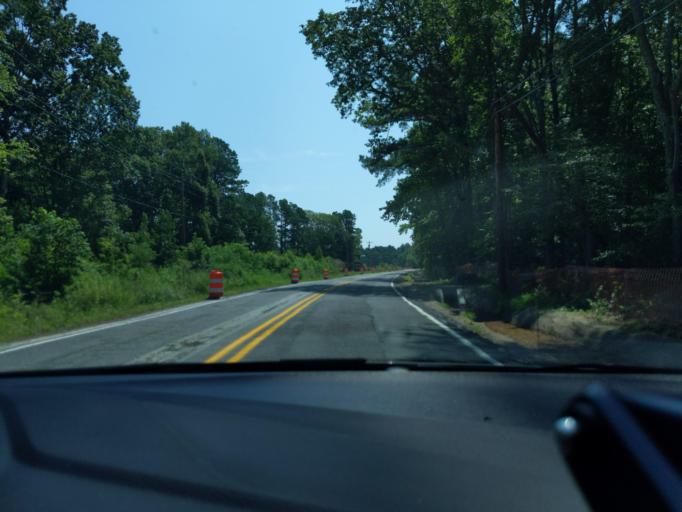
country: US
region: Virginia
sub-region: Northumberland County
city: Heathsville
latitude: 38.0767
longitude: -76.3484
